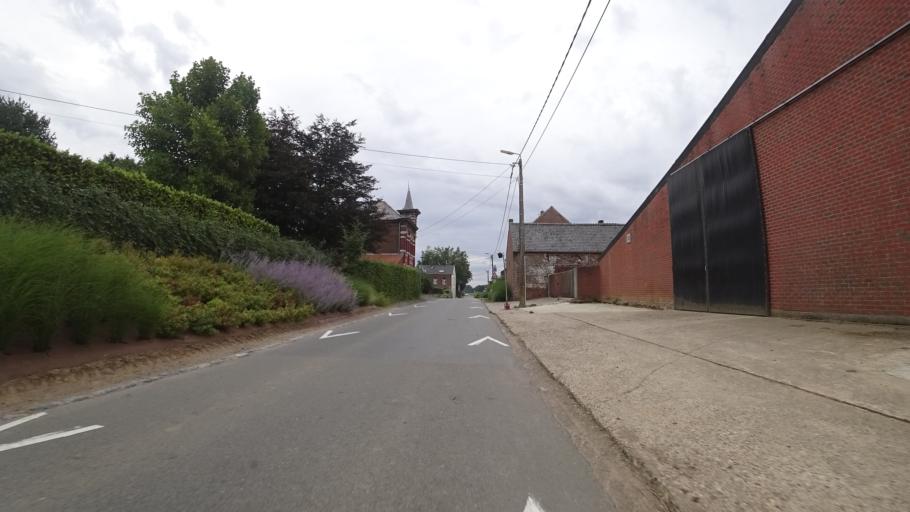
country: BE
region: Wallonia
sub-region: Province du Brabant Wallon
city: Walhain-Saint-Paul
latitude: 50.6025
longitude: 4.7468
